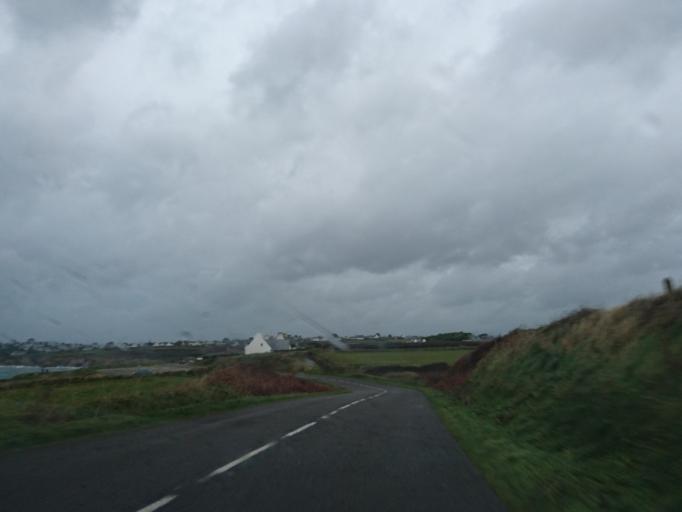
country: FR
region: Brittany
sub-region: Departement du Finistere
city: Le Conquet
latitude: 48.3422
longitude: -4.7714
